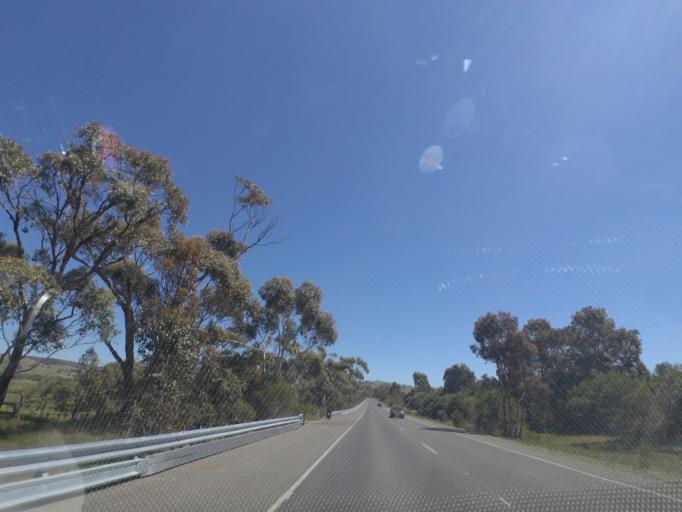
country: AU
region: Victoria
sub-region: Hume
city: Sunbury
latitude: -37.3041
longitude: 144.8332
